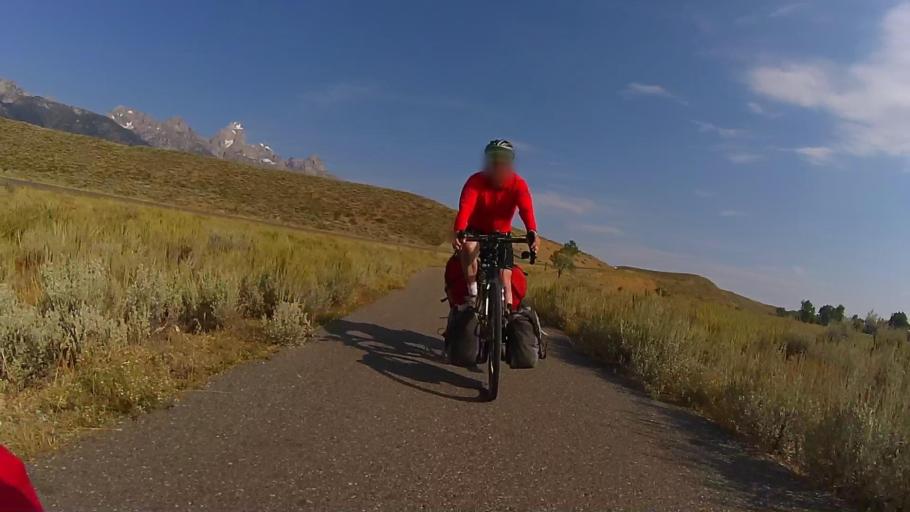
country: US
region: Wyoming
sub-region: Teton County
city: Moose Wilson Road
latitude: 43.6643
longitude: -110.7220
